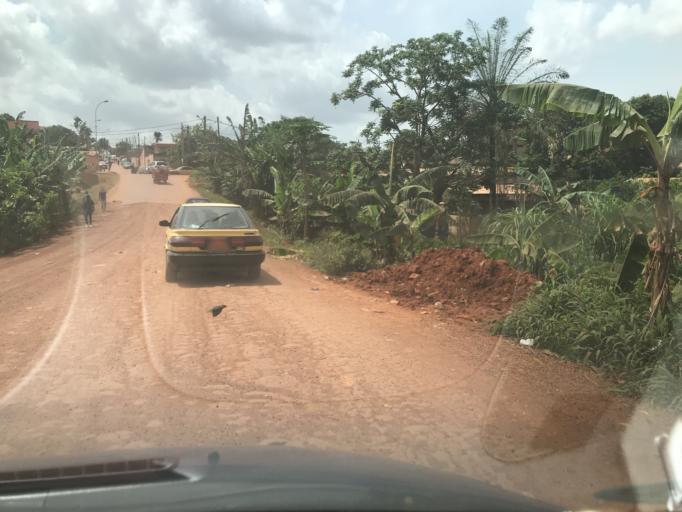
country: CM
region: Centre
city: Yaounde
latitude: 3.8475
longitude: 11.5325
